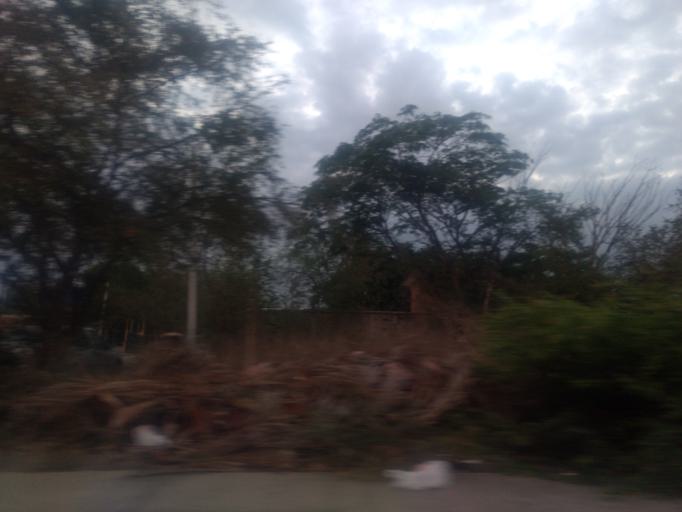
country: MX
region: Colima
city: Tapeixtles
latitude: 19.0893
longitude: -104.2911
